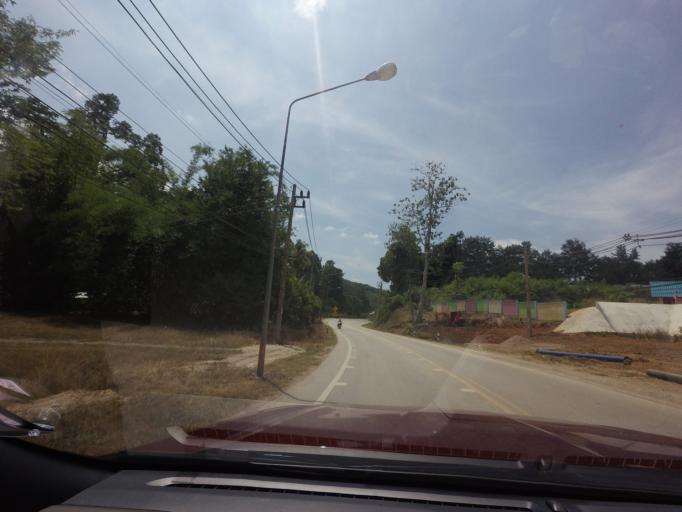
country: TH
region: Yala
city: Betong
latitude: 5.8153
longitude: 101.0884
